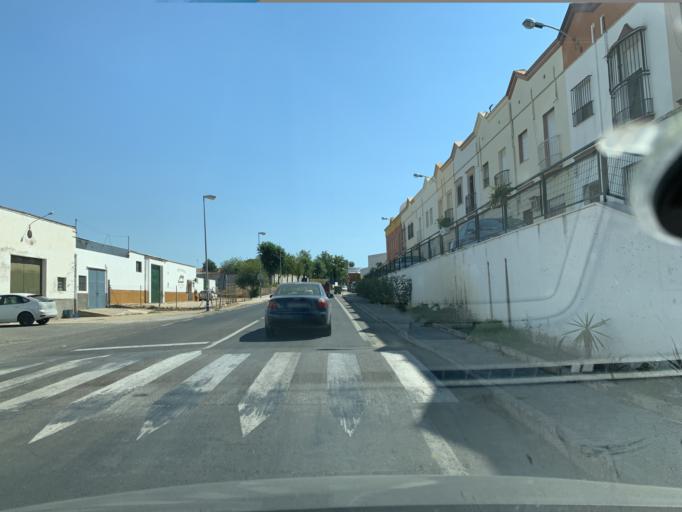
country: ES
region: Andalusia
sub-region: Provincia de Sevilla
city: Marchena
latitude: 37.3315
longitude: -5.4114
